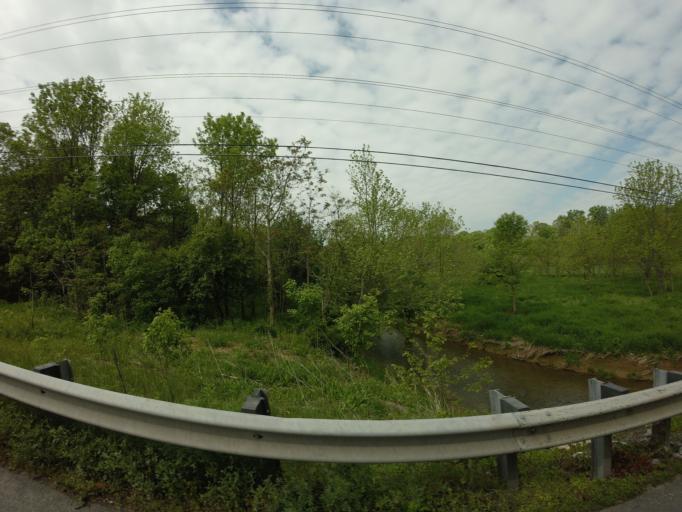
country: US
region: Maryland
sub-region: Frederick County
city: Urbana
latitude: 39.3173
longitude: -77.3334
